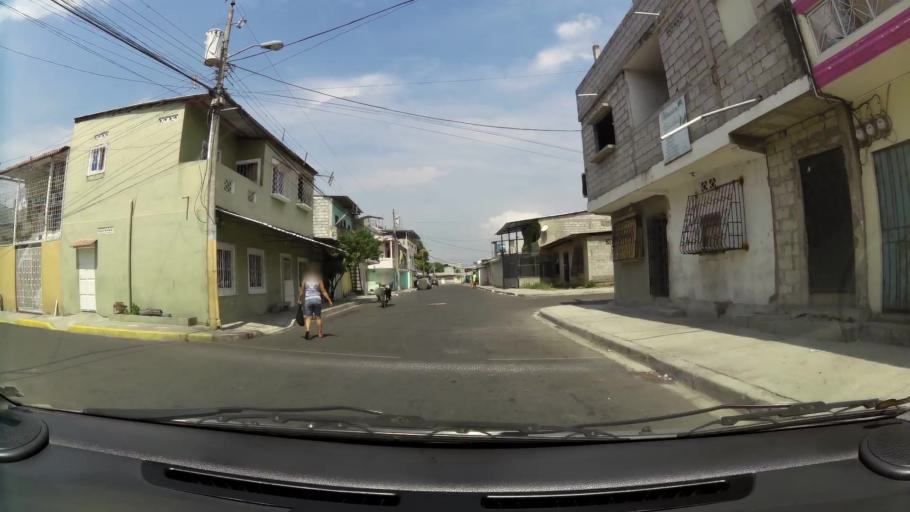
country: EC
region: Guayas
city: Guayaquil
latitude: -2.2646
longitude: -79.8724
